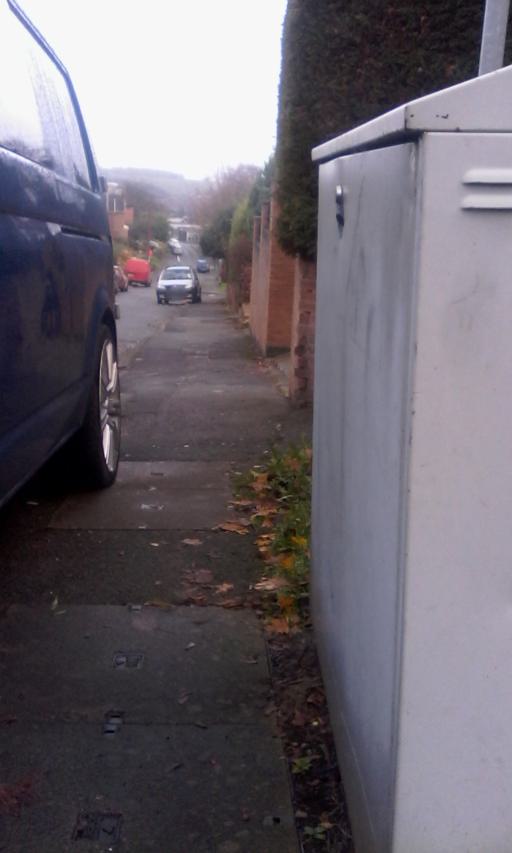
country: GB
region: England
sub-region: Nottinghamshire
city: Arnold
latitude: 52.9819
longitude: -1.1008
